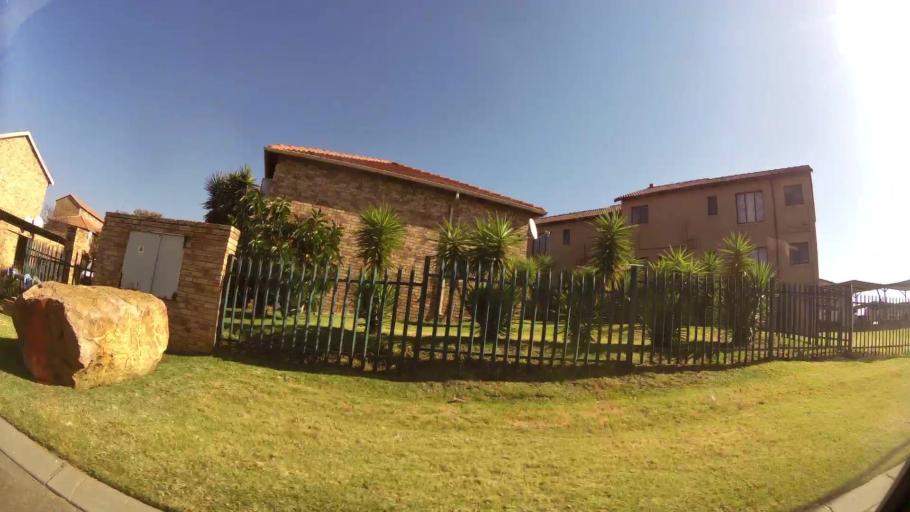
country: ZA
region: Gauteng
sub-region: Ekurhuleni Metropolitan Municipality
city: Germiston
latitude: -26.2475
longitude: 28.1136
